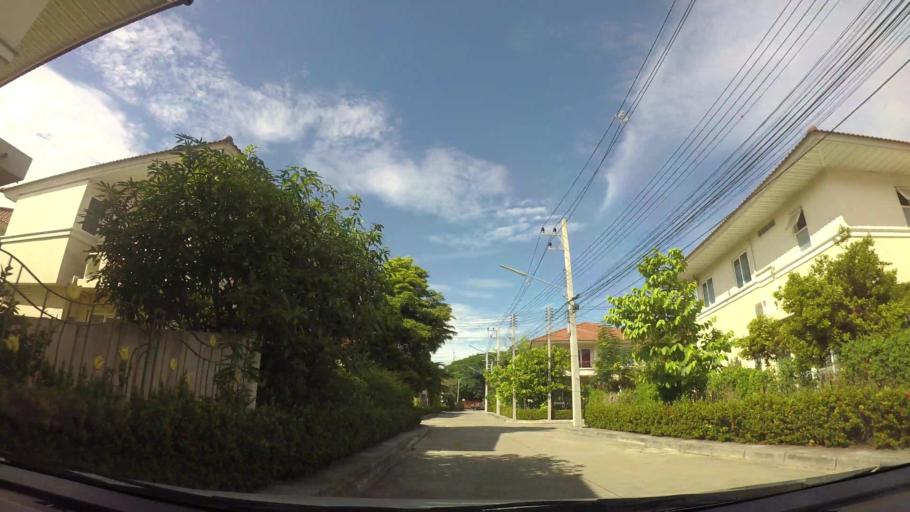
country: TH
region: Chiang Mai
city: Saraphi
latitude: 18.7560
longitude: 99.0340
